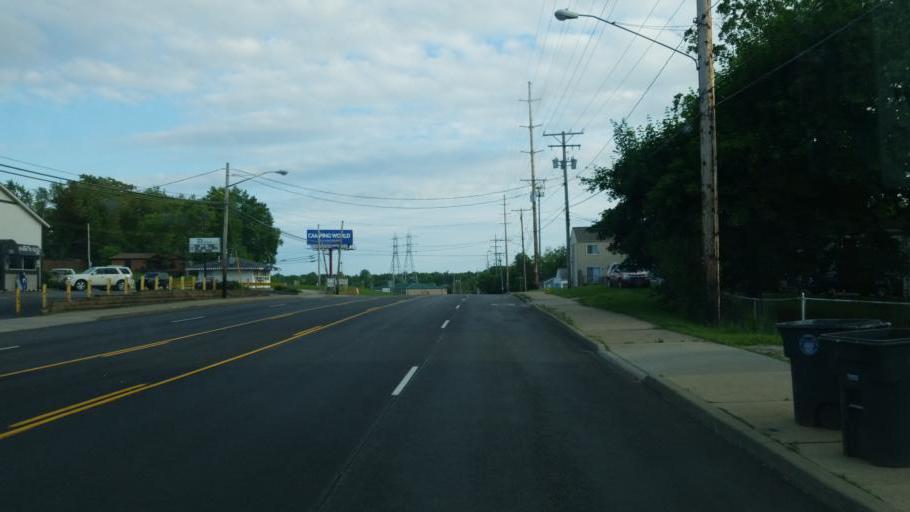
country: US
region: Ohio
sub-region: Summit County
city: Tallmadge
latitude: 41.0703
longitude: -81.4422
